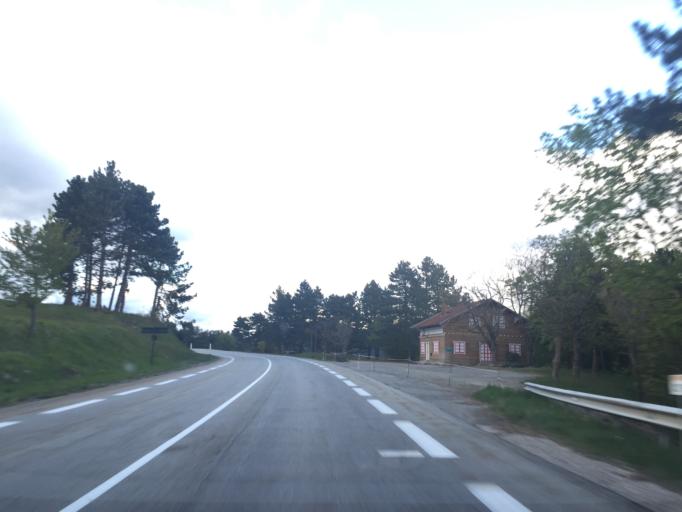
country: FR
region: Rhone-Alpes
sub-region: Departement de l'Isere
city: La Motte-Saint-Martin
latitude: 44.8748
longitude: 5.6252
